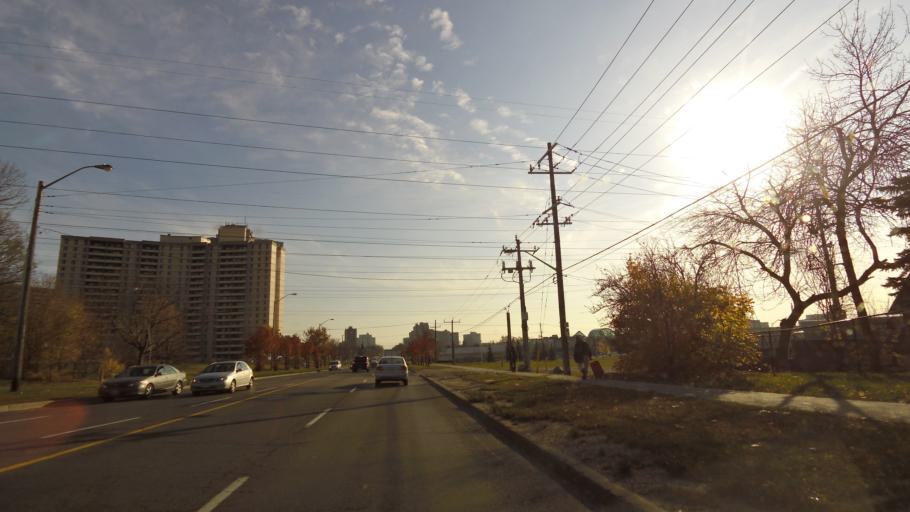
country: CA
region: Ontario
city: Concord
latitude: 43.7613
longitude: -79.5187
